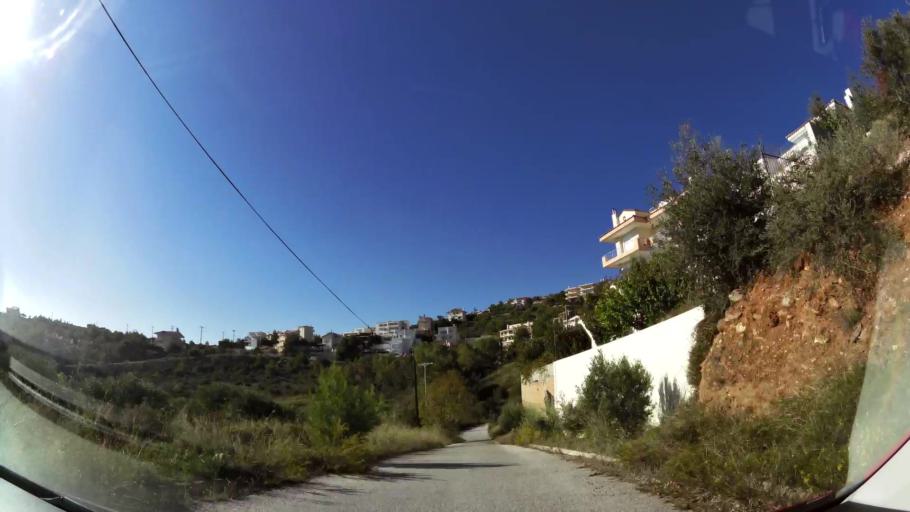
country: GR
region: Attica
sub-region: Nomarchia Anatolikis Attikis
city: Dhrafi
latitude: 38.0315
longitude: 23.8968
